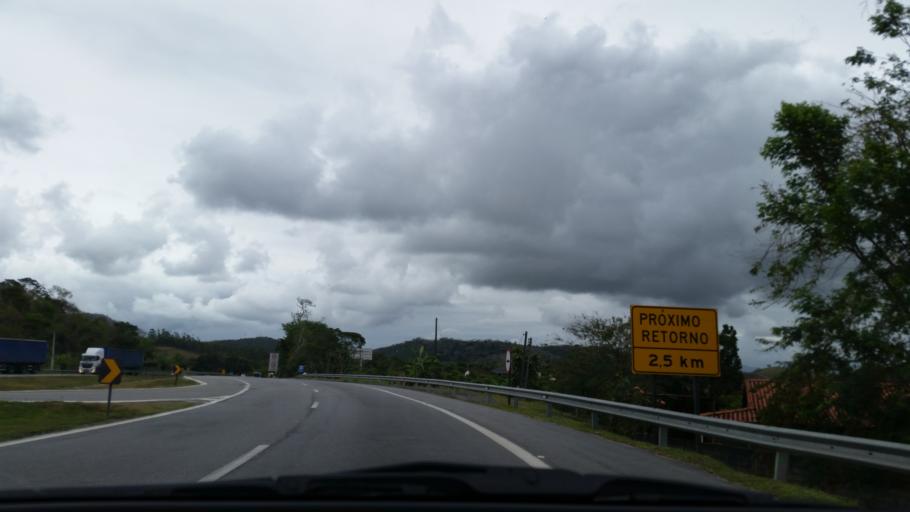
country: BR
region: Rio de Janeiro
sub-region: Saquarema
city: Saquarema
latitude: -22.8006
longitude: -42.4770
